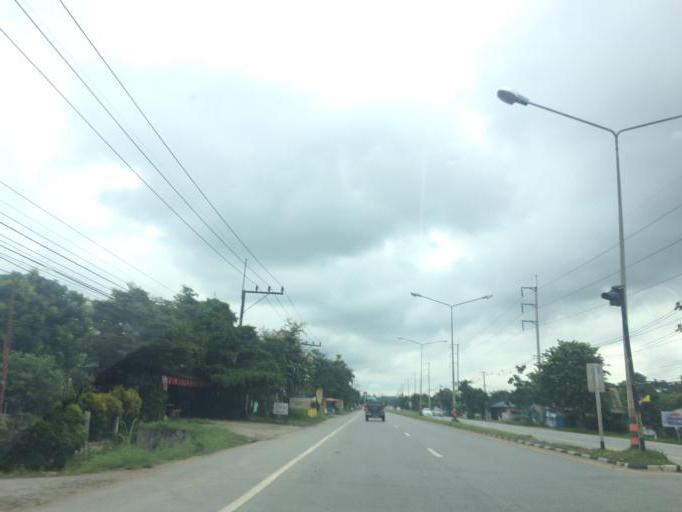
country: TH
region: Chiang Rai
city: Mae Chan
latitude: 20.0766
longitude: 99.8755
